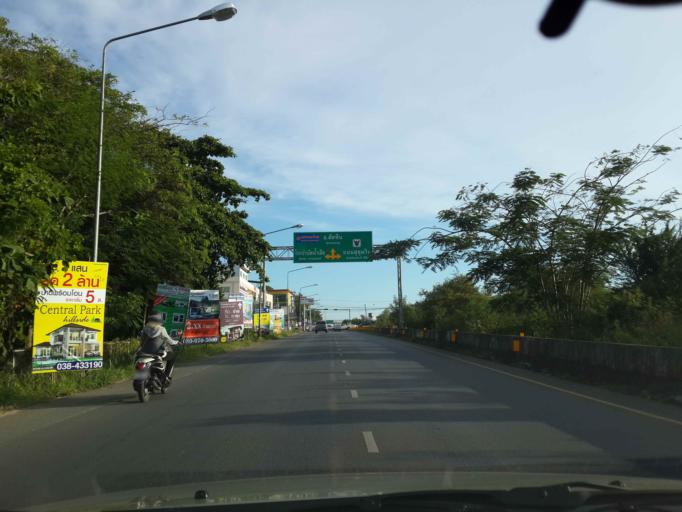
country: TH
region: Chon Buri
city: Phatthaya
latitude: 12.9505
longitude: 100.9149
